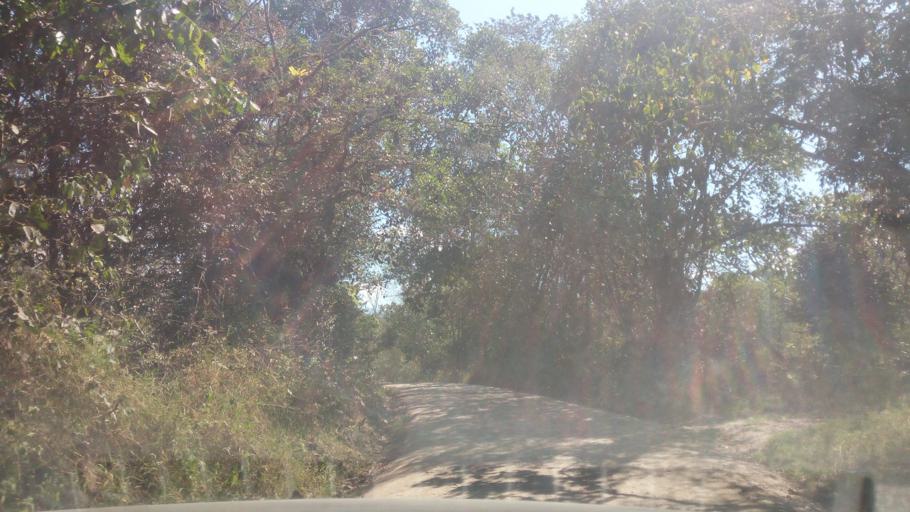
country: CO
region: Boyaca
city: Somondoco
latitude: 4.9815
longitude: -73.4412
